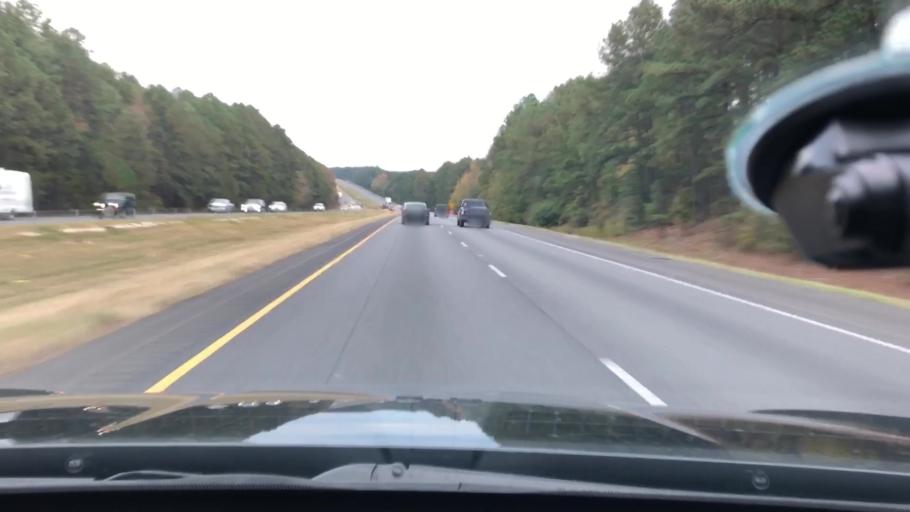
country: US
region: Arkansas
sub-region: Clark County
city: Arkadelphia
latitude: 34.2107
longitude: -93.0349
